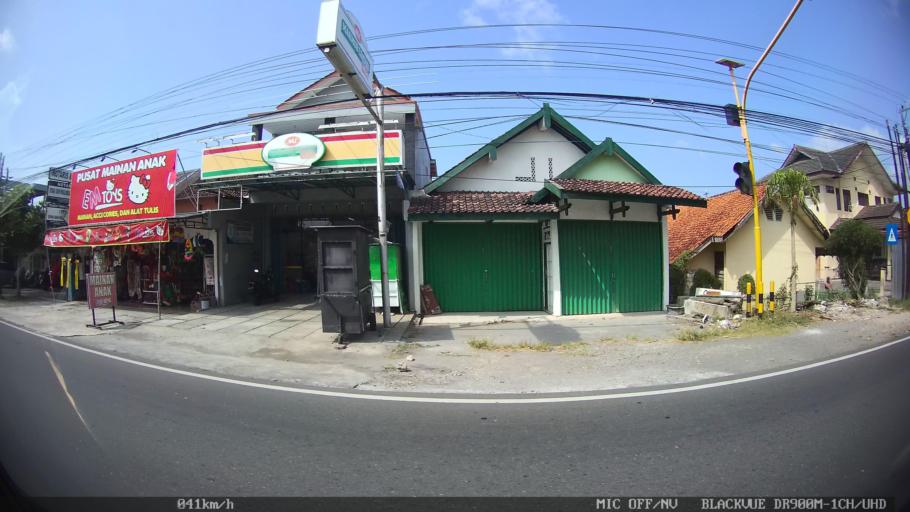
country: ID
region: Daerah Istimewa Yogyakarta
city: Srandakan
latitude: -7.8944
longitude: 110.1466
